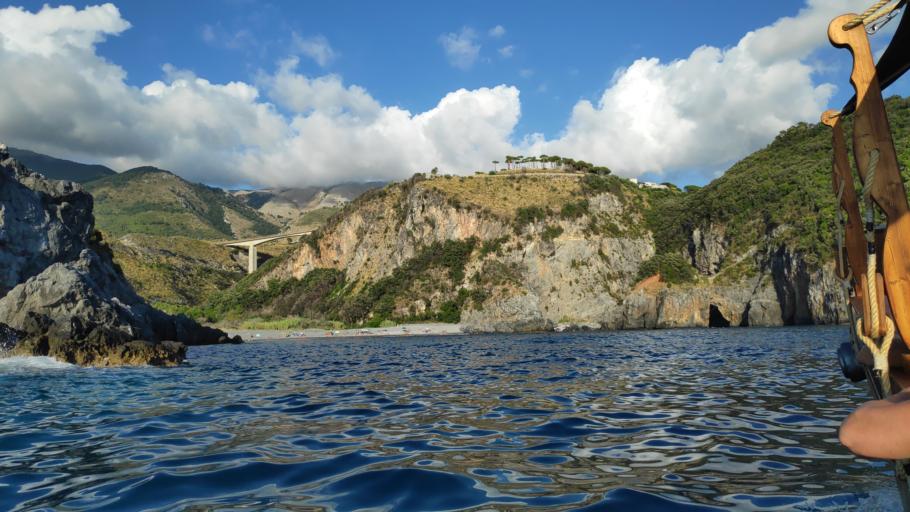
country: IT
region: Calabria
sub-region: Provincia di Cosenza
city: San Nicola Arcella
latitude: 39.8561
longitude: 15.7881
